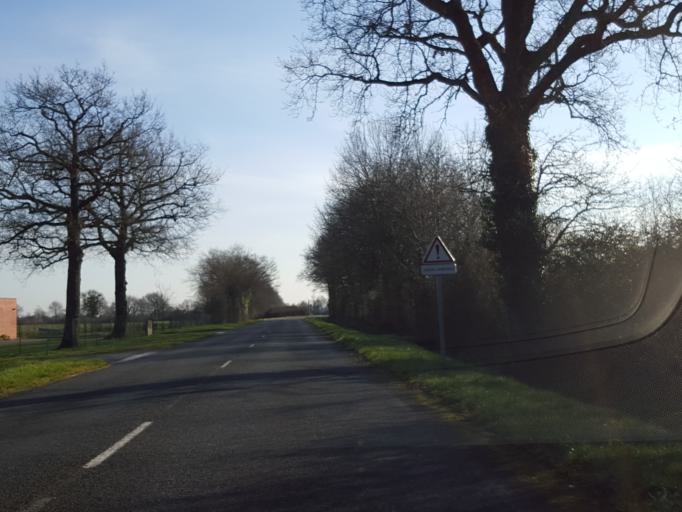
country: FR
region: Pays de la Loire
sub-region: Departement de la Vendee
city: La Chaize-le-Vicomte
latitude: 46.6705
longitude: -1.3139
